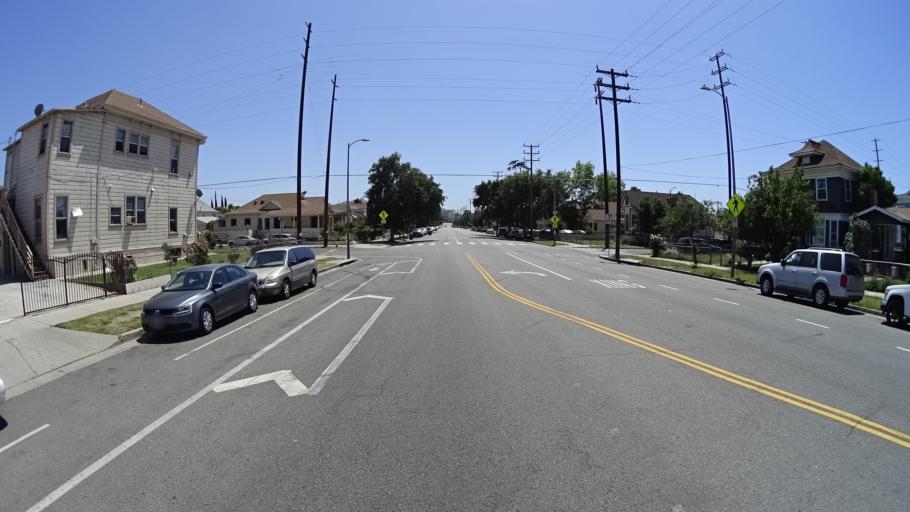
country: US
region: California
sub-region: Los Angeles County
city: Los Angeles
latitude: 34.0723
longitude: -118.2117
